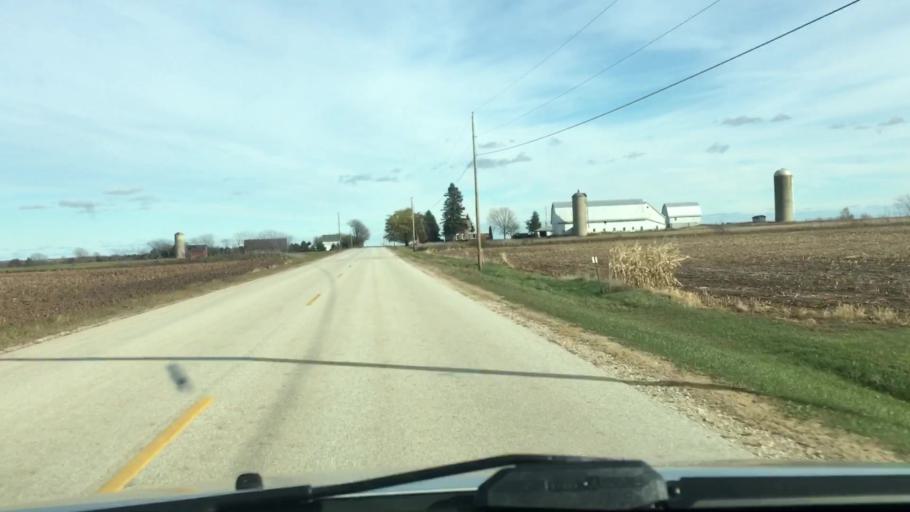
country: US
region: Wisconsin
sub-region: Kewaunee County
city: Algoma
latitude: 44.6974
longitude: -87.5920
